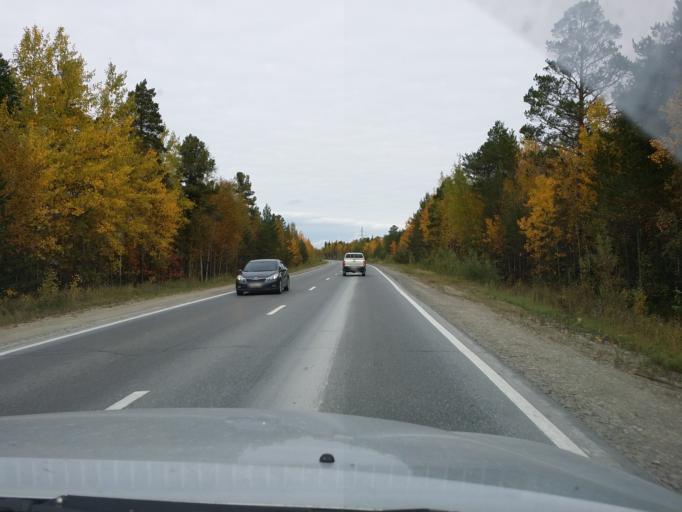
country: RU
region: Khanty-Mansiyskiy Avtonomnyy Okrug
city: Megion
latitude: 61.1398
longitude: 75.7619
